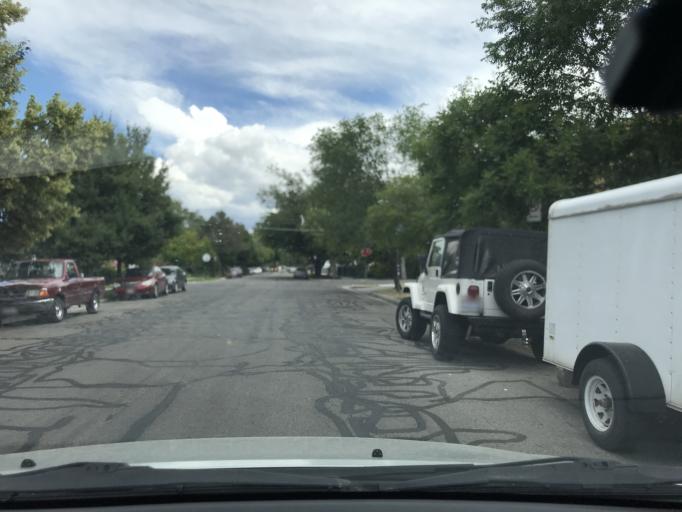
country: US
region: Utah
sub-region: Salt Lake County
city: Salt Lake City
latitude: 40.7798
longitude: -111.9284
